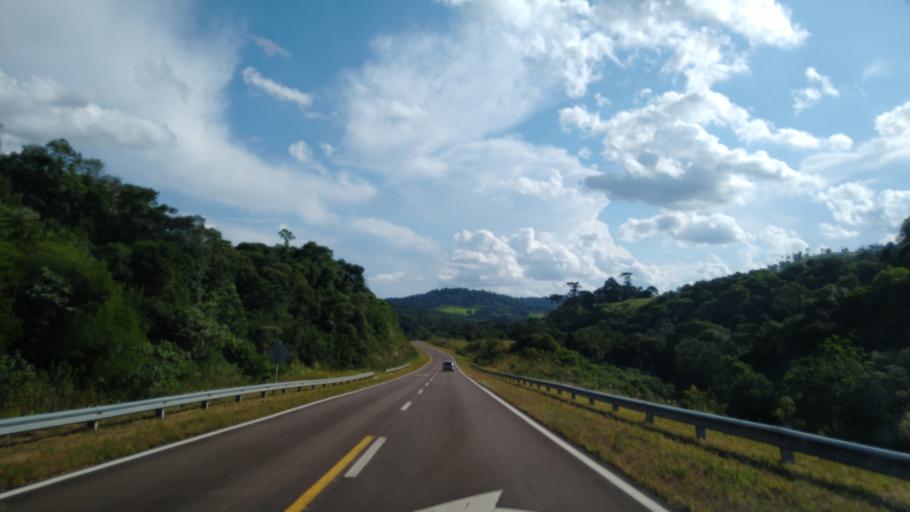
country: AR
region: Misiones
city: Bernardo de Irigoyen
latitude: -26.3234
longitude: -53.7556
